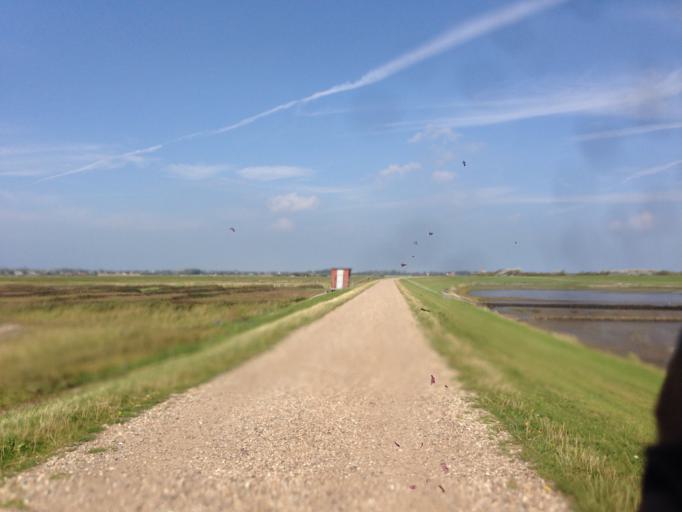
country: DE
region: Schleswig-Holstein
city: Tinnum
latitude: 54.8783
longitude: 8.3369
